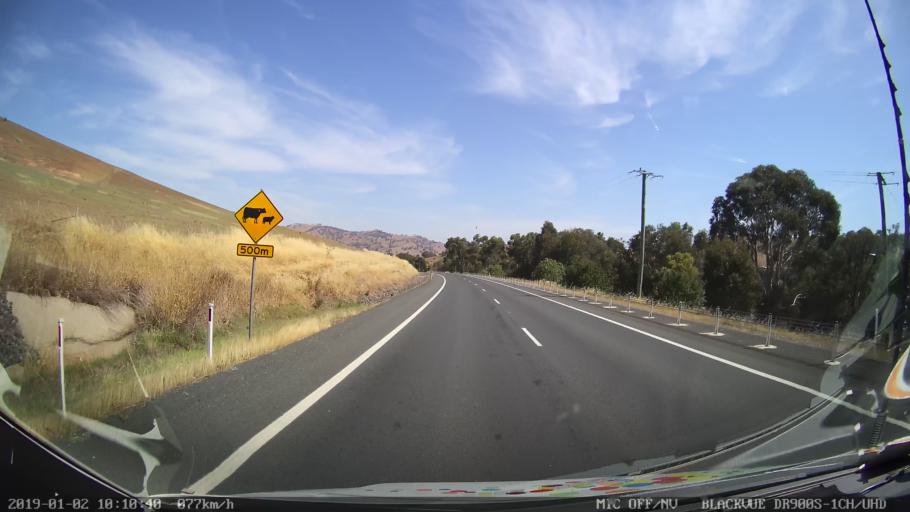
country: AU
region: New South Wales
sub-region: Gundagai
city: Gundagai
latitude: -35.1010
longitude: 148.0959
